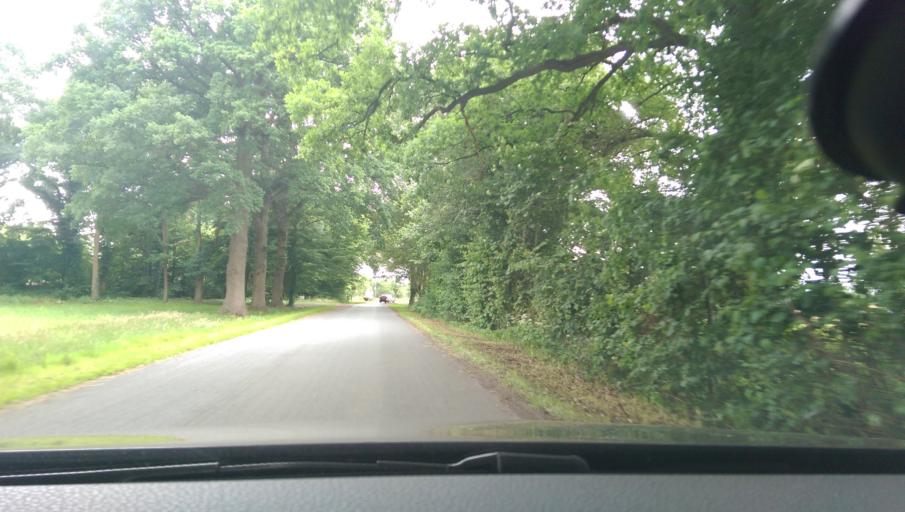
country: DE
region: Lower Saxony
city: Horstedt
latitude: 53.1763
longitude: 9.2386
